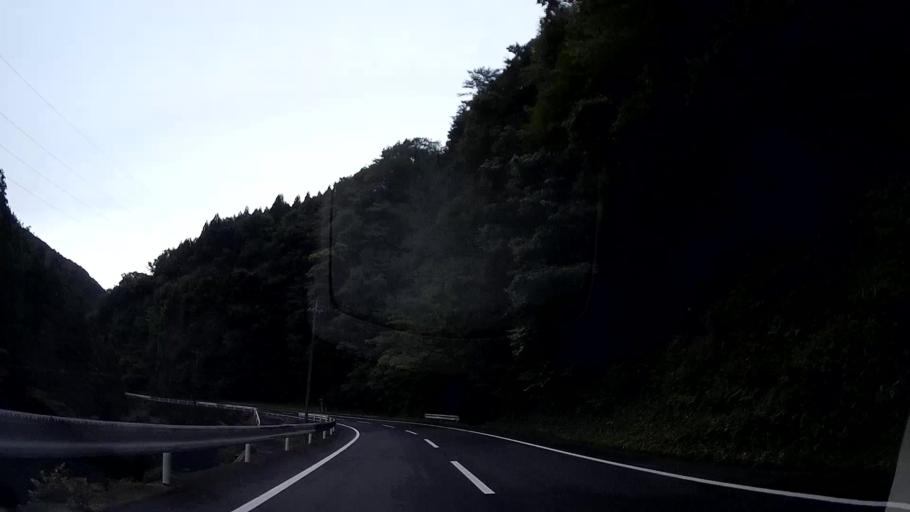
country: JP
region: Kumamoto
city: Kikuchi
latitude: 33.0709
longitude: 130.9152
